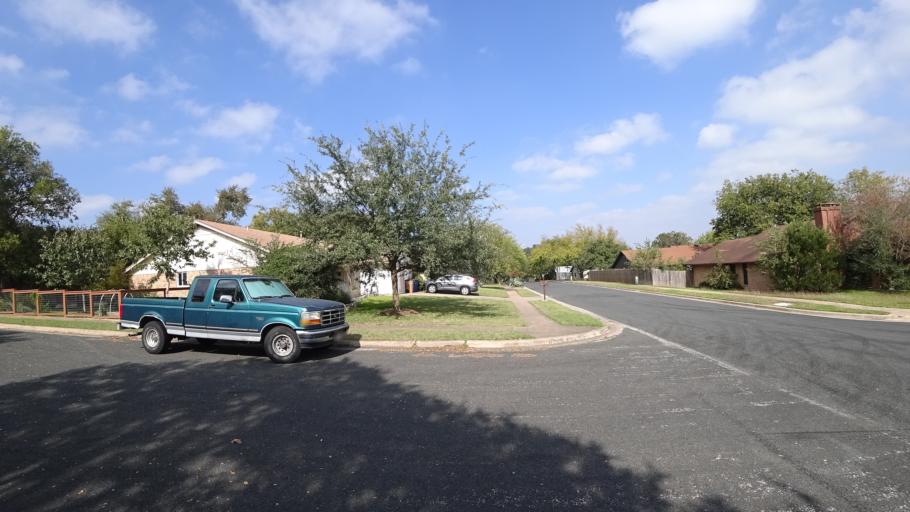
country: US
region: Texas
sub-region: Travis County
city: Shady Hollow
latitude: 30.2050
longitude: -97.8199
